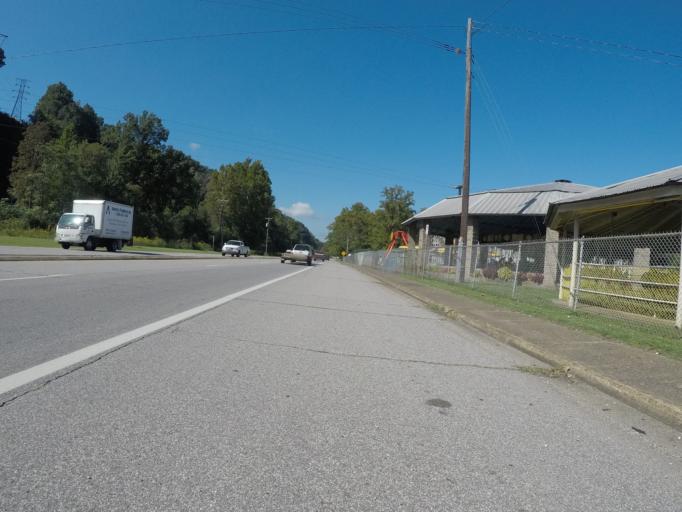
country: US
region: Ohio
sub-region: Lawrence County
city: Burlington
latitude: 38.3967
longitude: -82.5304
